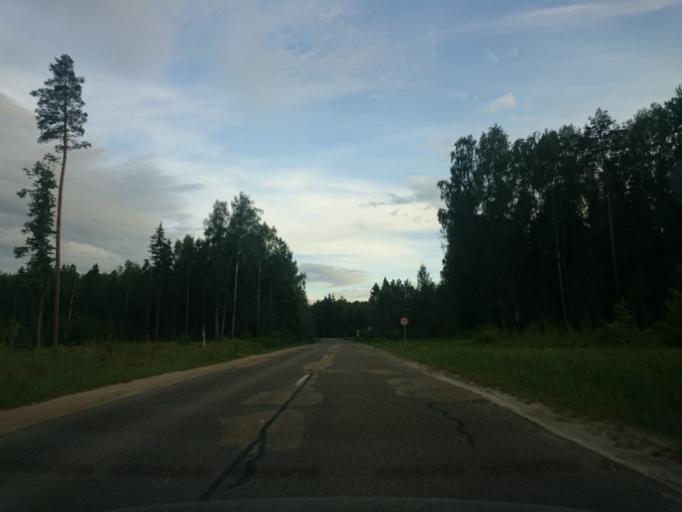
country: LV
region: Ropazu
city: Ropazi
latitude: 57.0130
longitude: 24.6815
